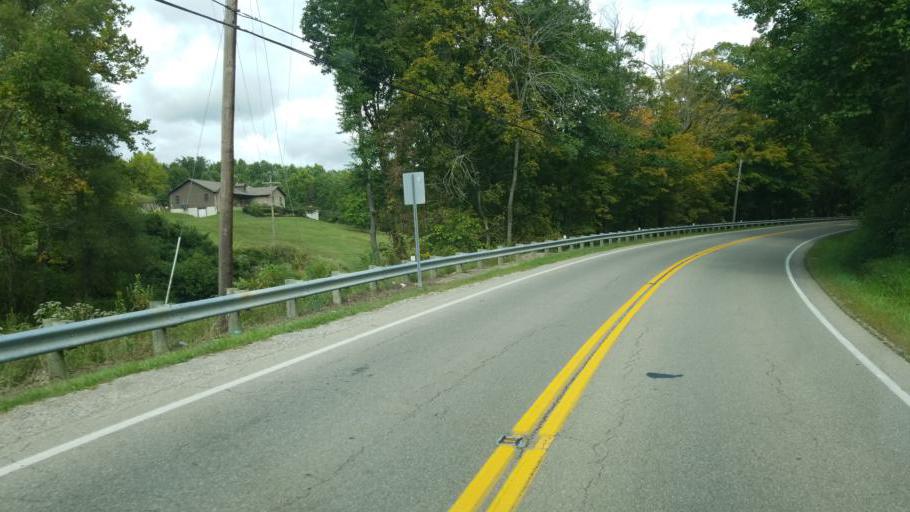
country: US
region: Ohio
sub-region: Jackson County
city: Oak Hill
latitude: 38.8965
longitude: -82.5909
